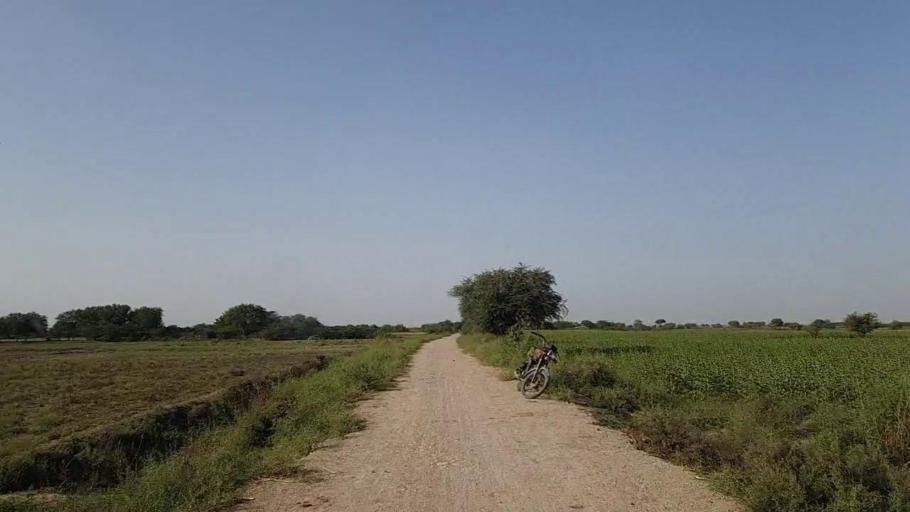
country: PK
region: Sindh
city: Jati
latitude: 24.2875
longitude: 68.1491
